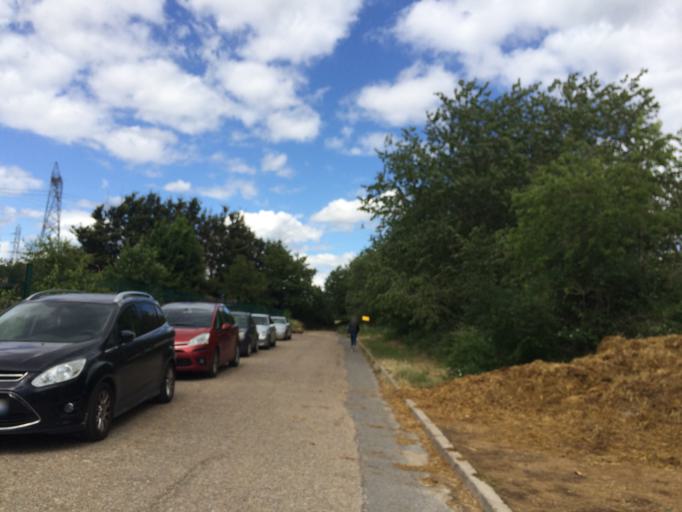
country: FR
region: Ile-de-France
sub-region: Departement de l'Essonne
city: Les Ulis
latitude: 48.6734
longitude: 2.1819
